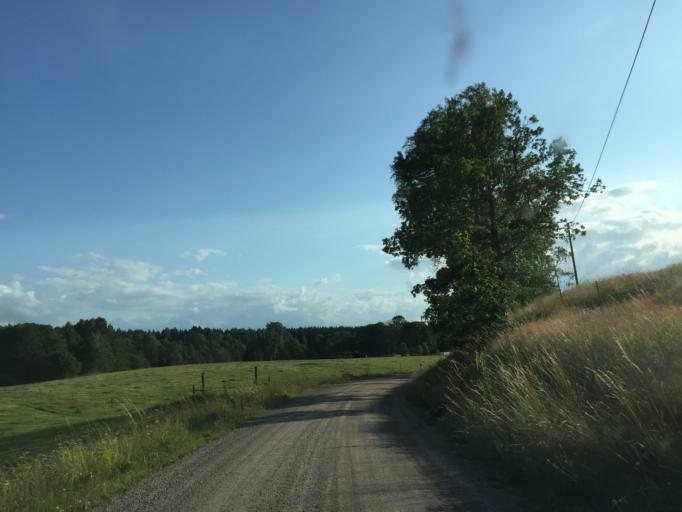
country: SE
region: OEstergoetland
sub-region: Motala Kommun
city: Ryd
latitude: 58.6867
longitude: 14.9904
